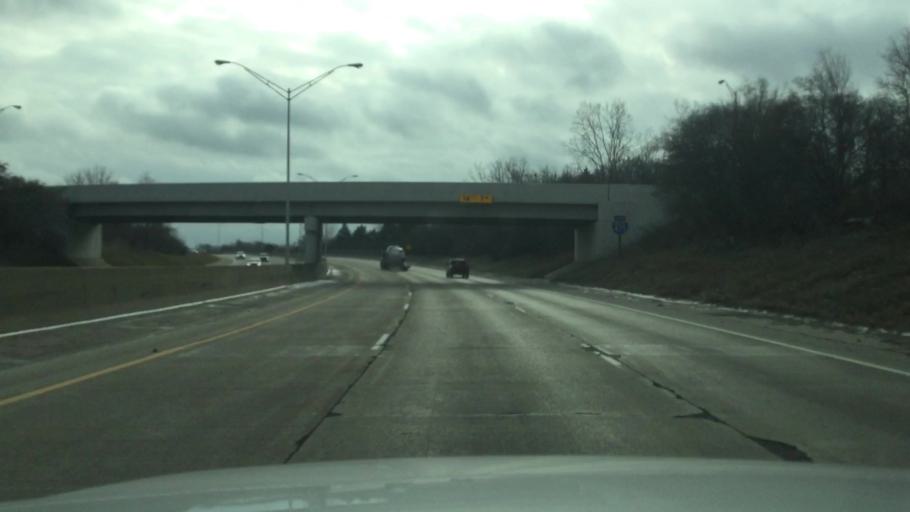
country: US
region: Michigan
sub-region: Genesee County
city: Beecher
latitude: 43.0677
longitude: -83.6835
